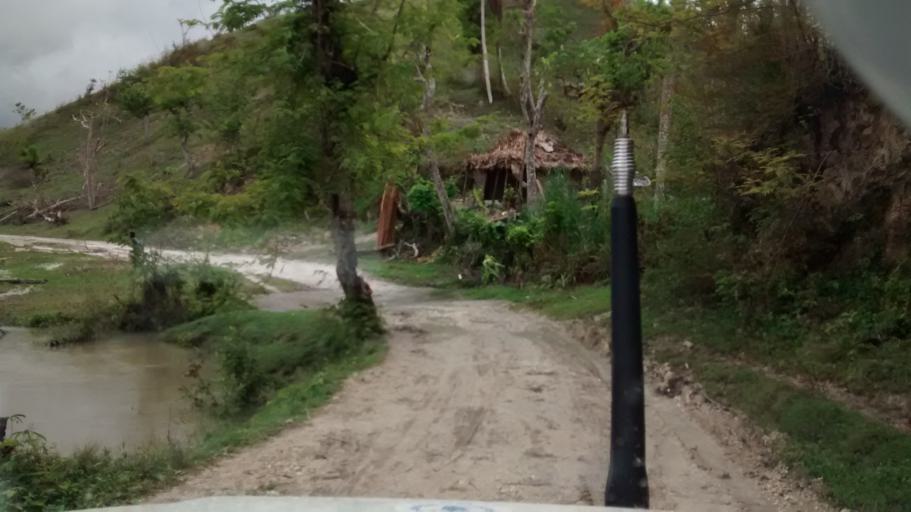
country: HT
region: Grandans
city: Jeremie
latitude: 18.5755
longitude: -74.1520
